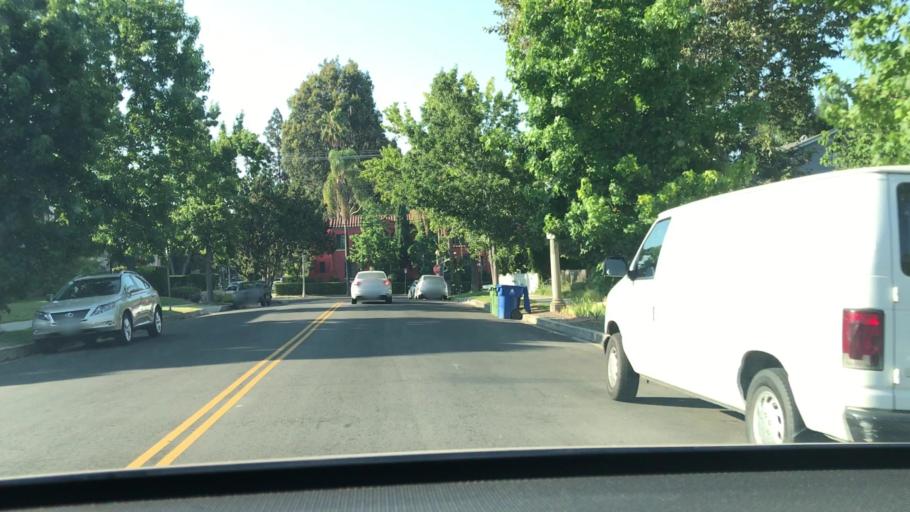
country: US
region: California
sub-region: Los Angeles County
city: Hollywood
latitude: 34.0646
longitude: -118.3171
